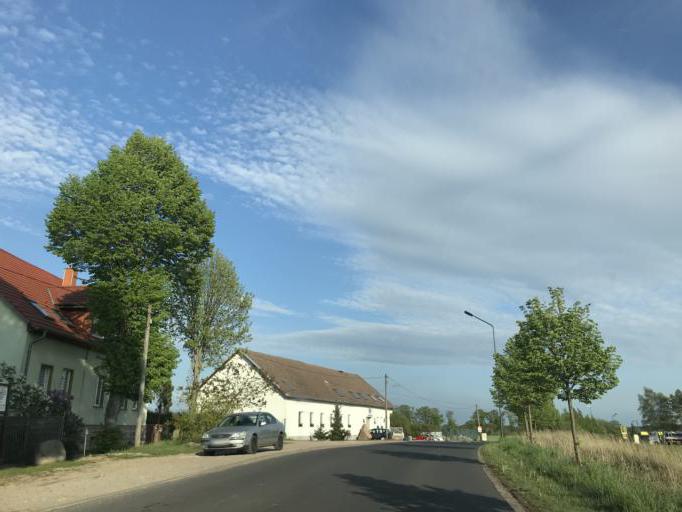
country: DE
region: Brandenburg
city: Joachimsthal
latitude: 52.9712
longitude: 13.7468
